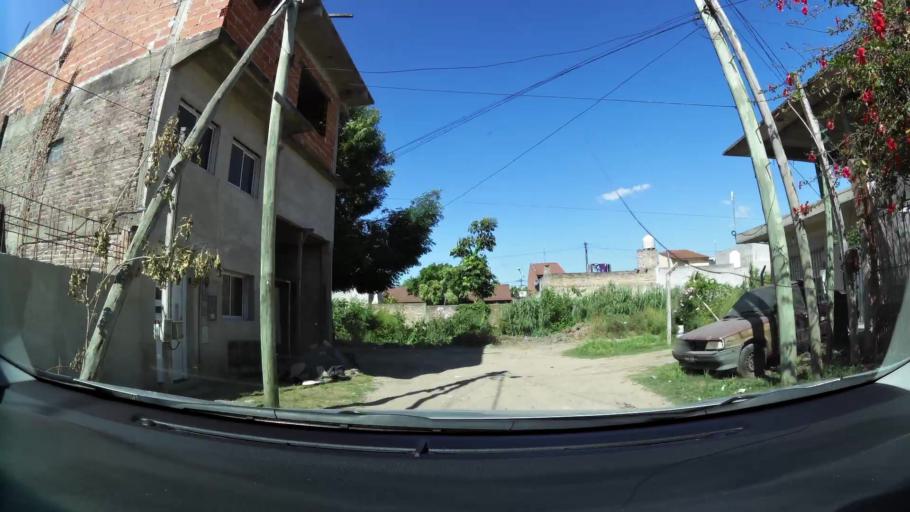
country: AR
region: Buenos Aires F.D.
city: Villa Lugano
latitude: -34.7062
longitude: -58.4757
